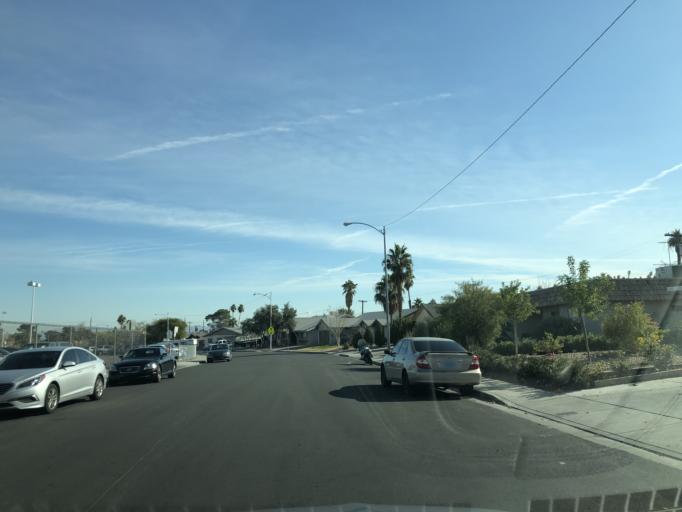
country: US
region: Nevada
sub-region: Clark County
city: Winchester
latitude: 36.1249
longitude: -115.1316
